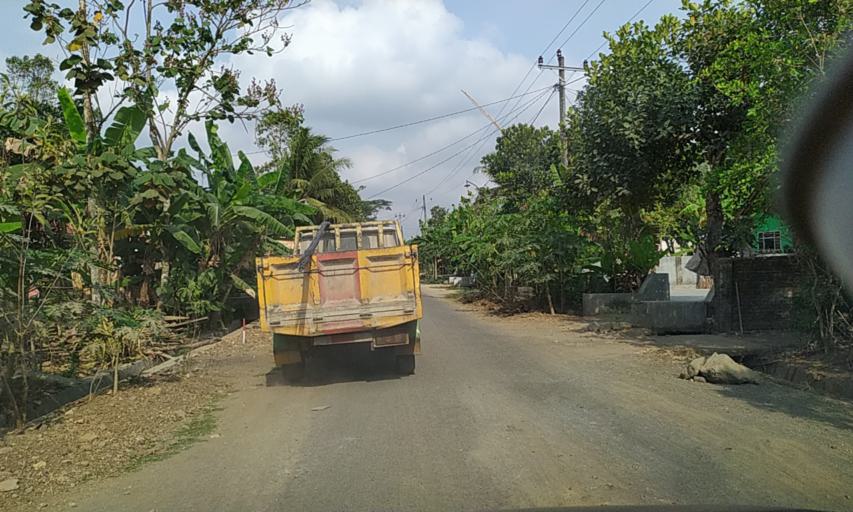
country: ID
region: Central Java
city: Kedungwringin
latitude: -7.4738
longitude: 108.7669
